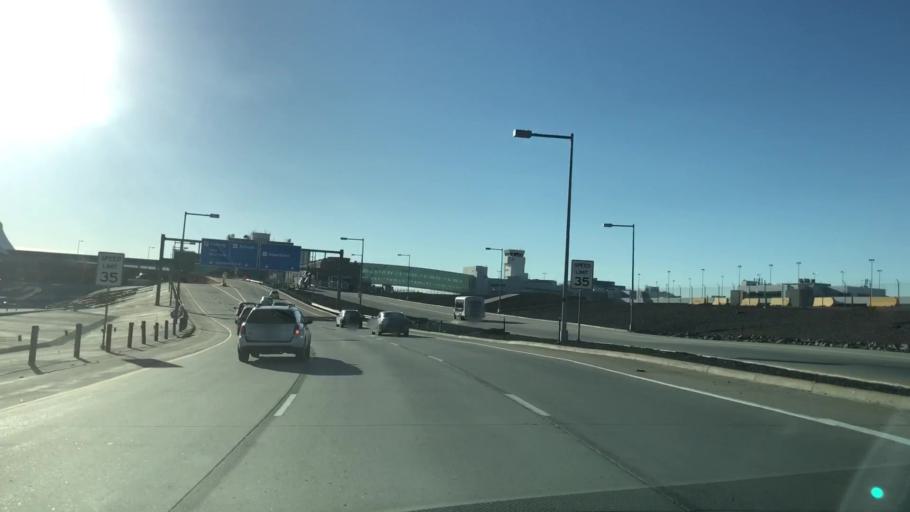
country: US
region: Colorado
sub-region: Weld County
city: Lochbuie
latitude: 39.8510
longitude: -104.6668
